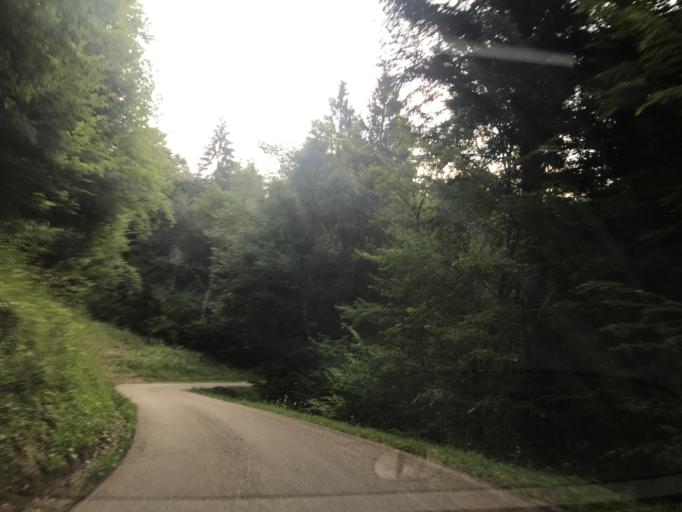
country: FR
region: Rhone-Alpes
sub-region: Departement de l'Isere
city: Saint-Vincent-de-Mercuze
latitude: 45.3956
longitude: 5.9371
